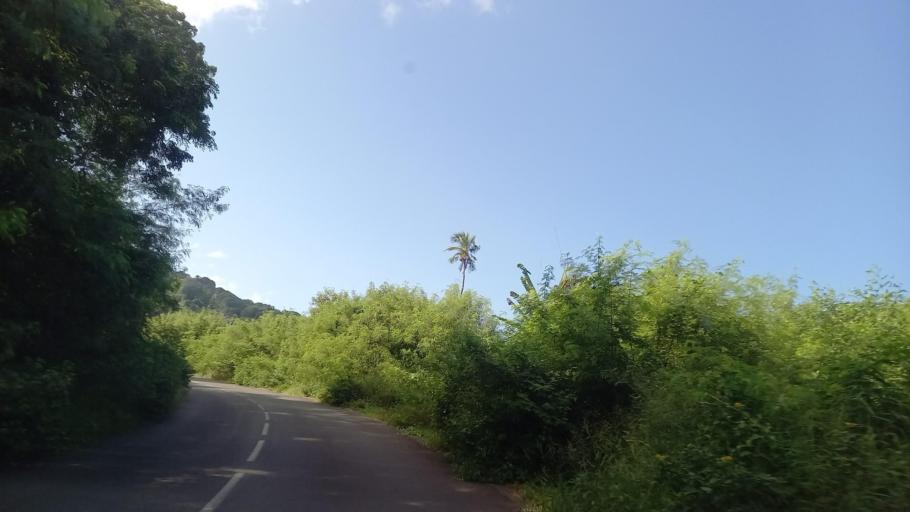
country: YT
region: Kani-Keli
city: Kani Keli
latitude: -12.9865
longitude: 45.1370
